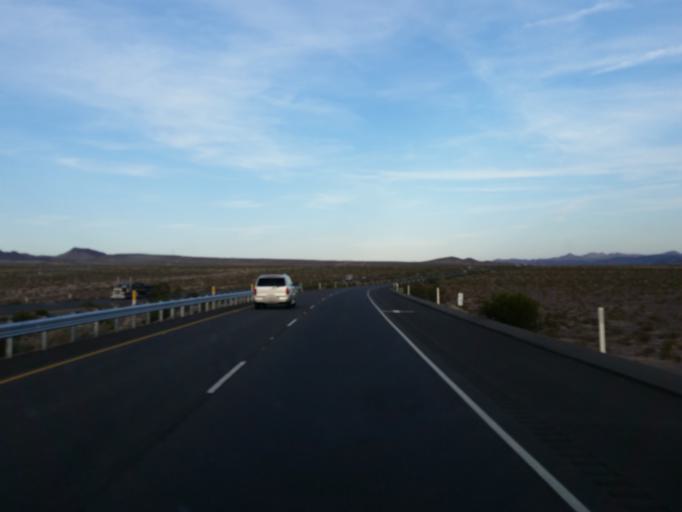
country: US
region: California
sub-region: San Bernardino County
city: Fort Irwin
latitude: 34.7718
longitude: -116.3663
